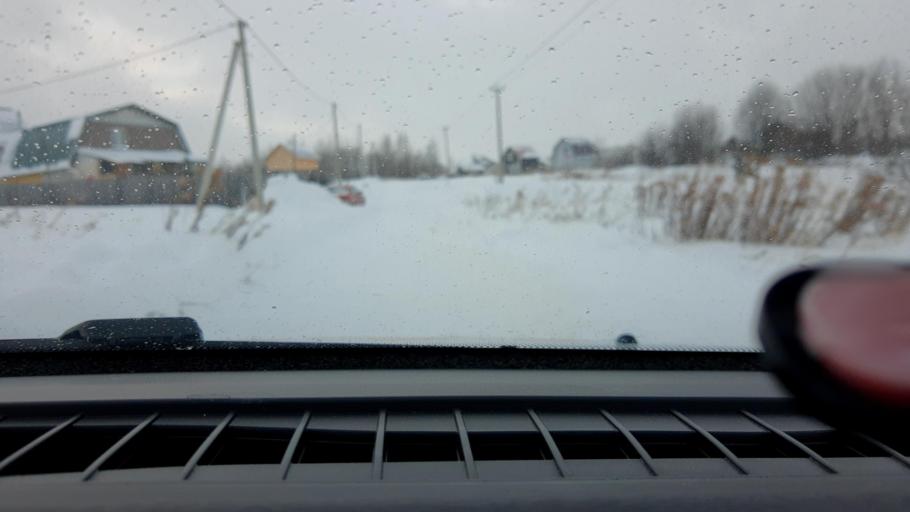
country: RU
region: Nizjnij Novgorod
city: Burevestnik
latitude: 56.1496
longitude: 43.7422
